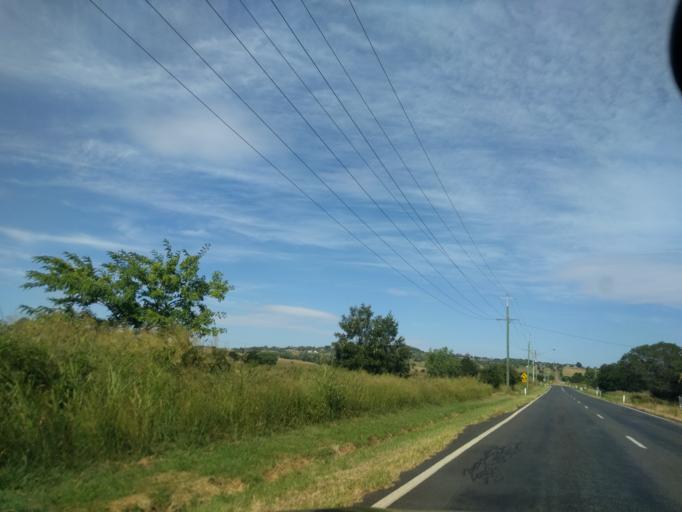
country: AU
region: Queensland
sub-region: Ipswich
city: Thagoona
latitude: -27.5749
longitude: 152.5945
